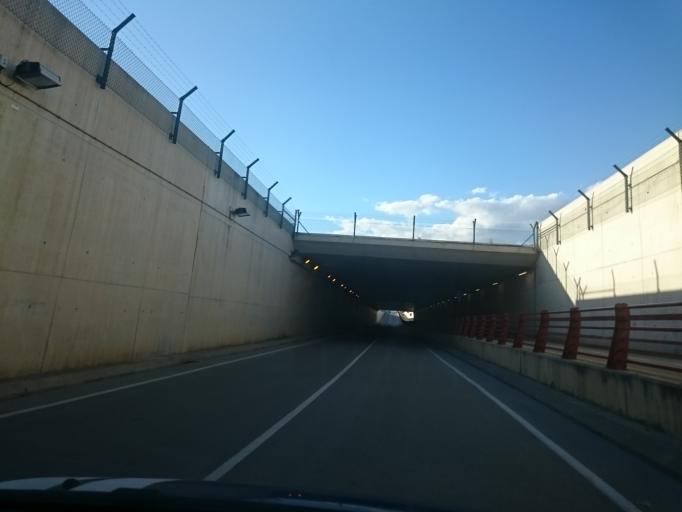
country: ES
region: Catalonia
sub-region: Provincia de Barcelona
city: El Prat de Llobregat
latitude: 41.2917
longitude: 2.1047
